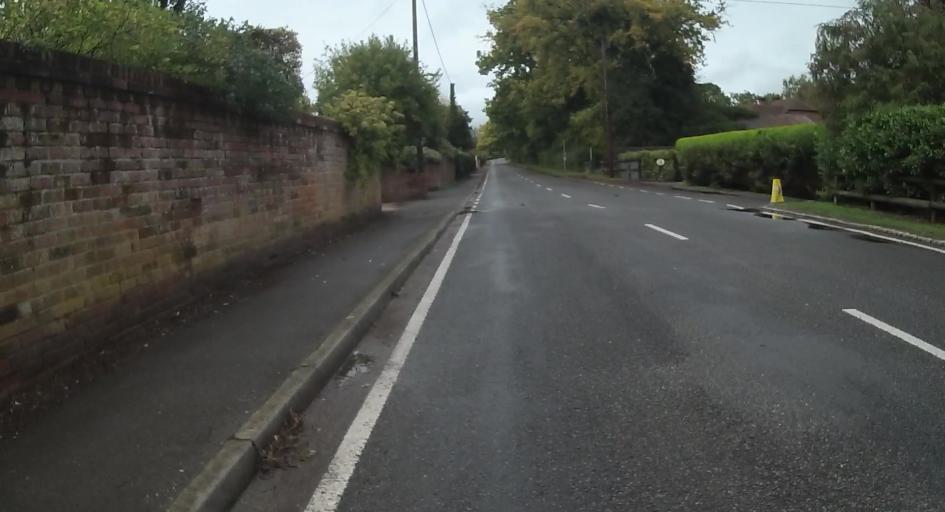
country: GB
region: England
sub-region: Hampshire
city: Tadley
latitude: 51.3497
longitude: -1.1661
